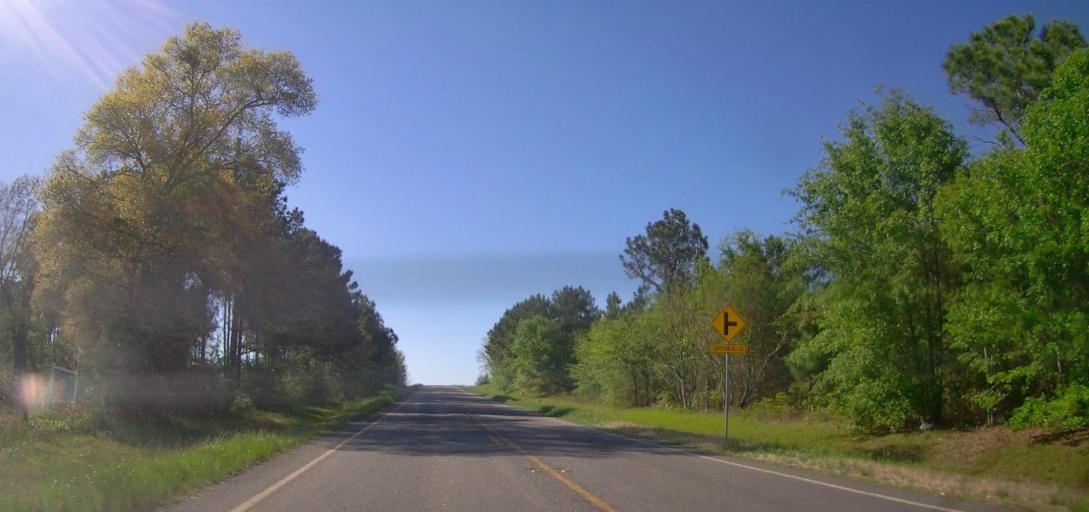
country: US
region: Georgia
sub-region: Wilcox County
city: Rochelle
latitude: 31.9878
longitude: -83.4640
